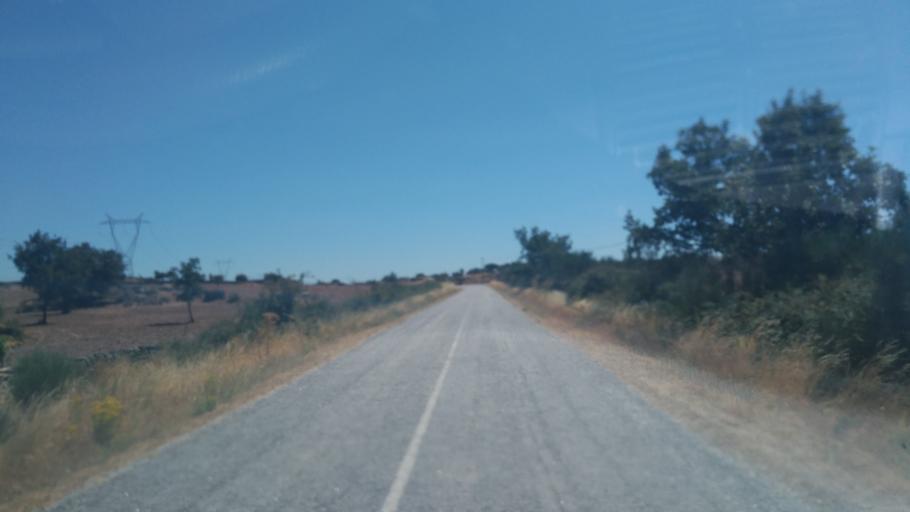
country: ES
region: Castille and Leon
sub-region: Provincia de Salamanca
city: Aldeadavila de la Ribera
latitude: 41.2072
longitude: -6.6419
